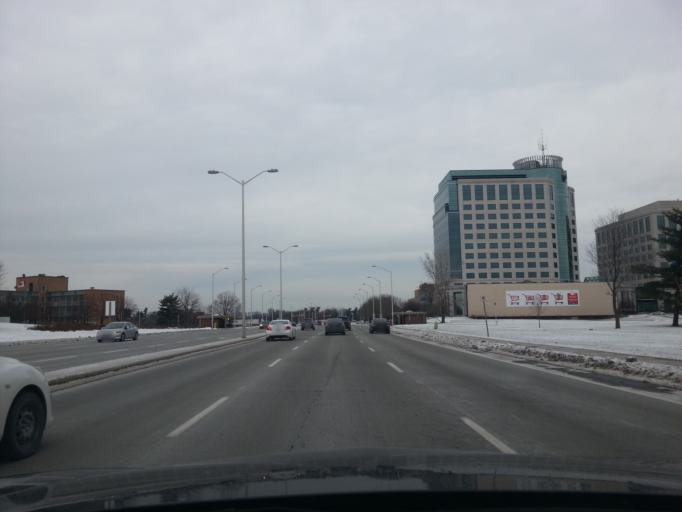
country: CA
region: Ontario
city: Ottawa
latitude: 45.3740
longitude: -75.6910
